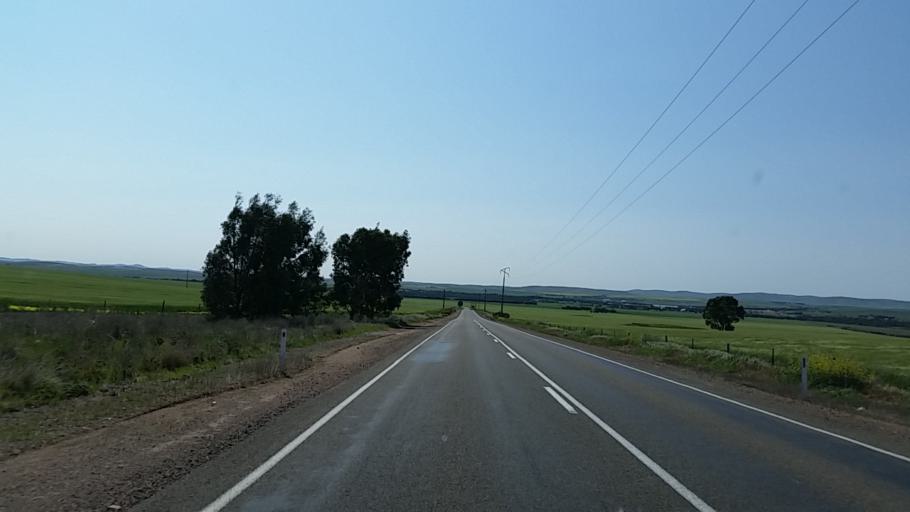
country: AU
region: South Australia
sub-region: Port Pirie City and Dists
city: Crystal Brook
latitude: -33.2775
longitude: 138.2980
